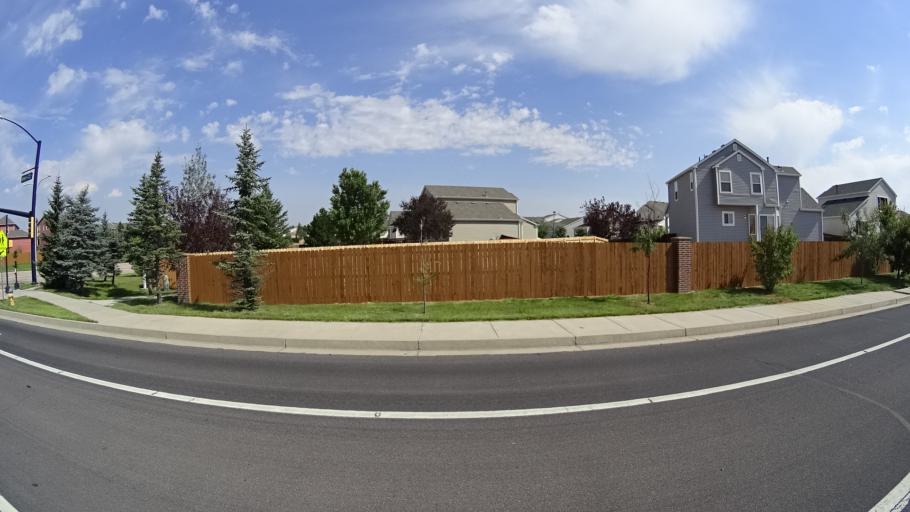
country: US
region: Colorado
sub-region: El Paso County
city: Cimarron Hills
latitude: 38.9262
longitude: -104.6989
